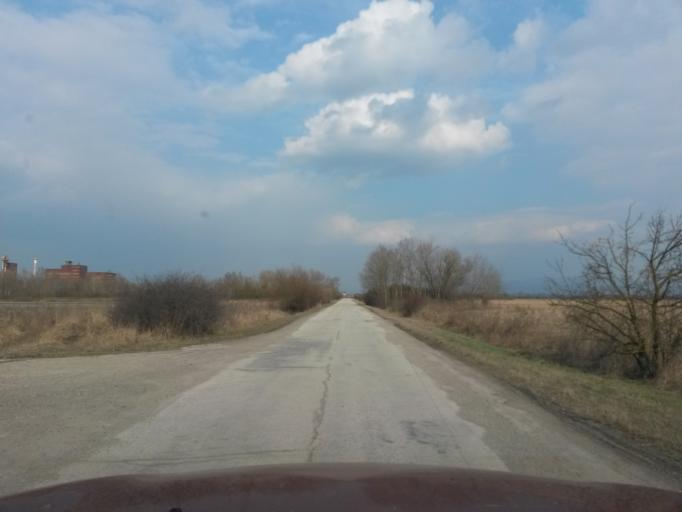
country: HU
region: Borsod-Abauj-Zemplen
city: Gonc
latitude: 48.5767
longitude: 21.2045
